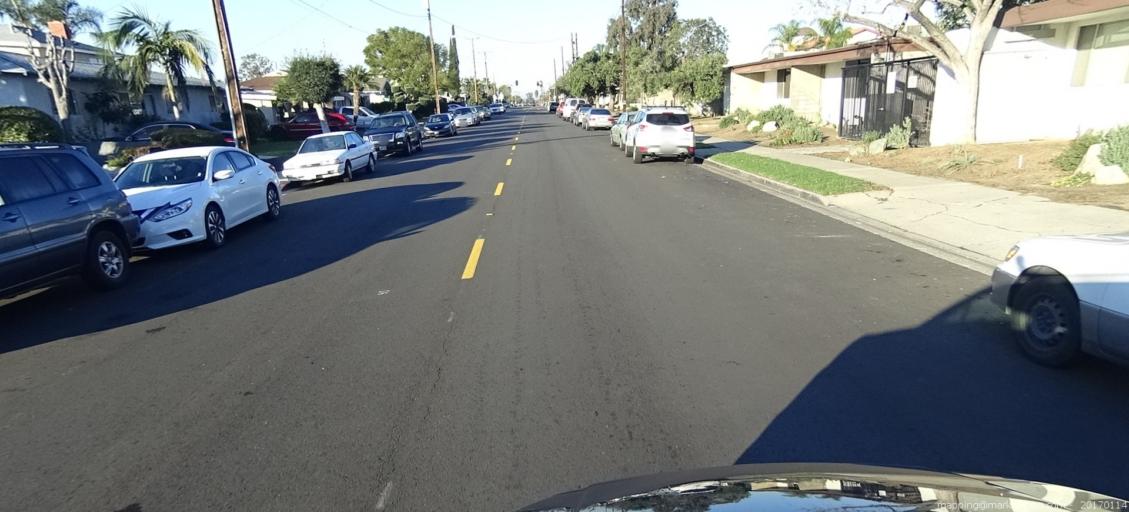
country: US
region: California
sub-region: Orange County
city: Villa Park
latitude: 33.7914
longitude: -117.8033
